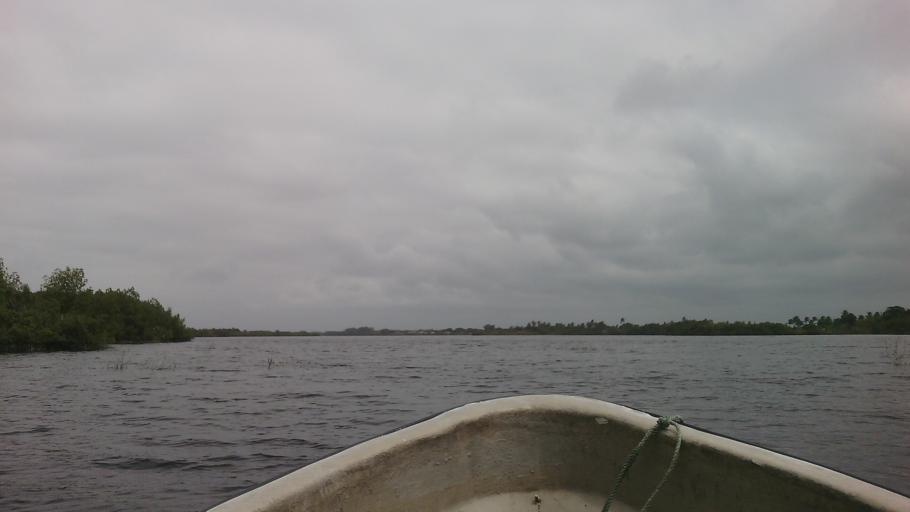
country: BJ
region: Atlantique
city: Hevie
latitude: 6.3502
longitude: 2.2874
